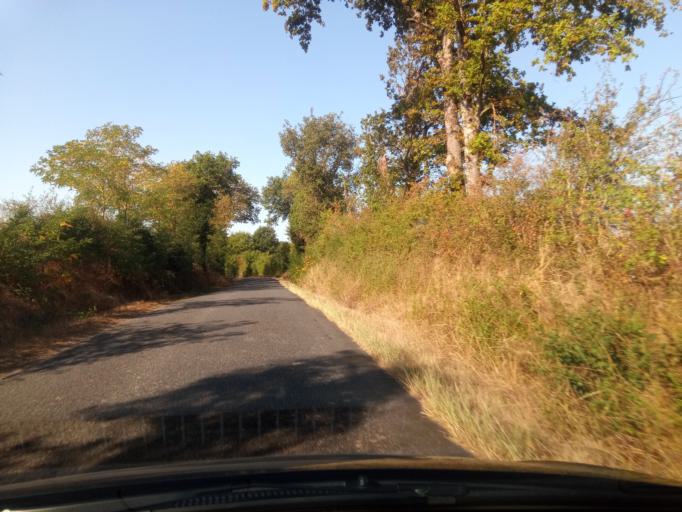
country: FR
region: Poitou-Charentes
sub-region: Departement de la Vienne
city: Saulge
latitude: 46.3310
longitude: 0.8576
